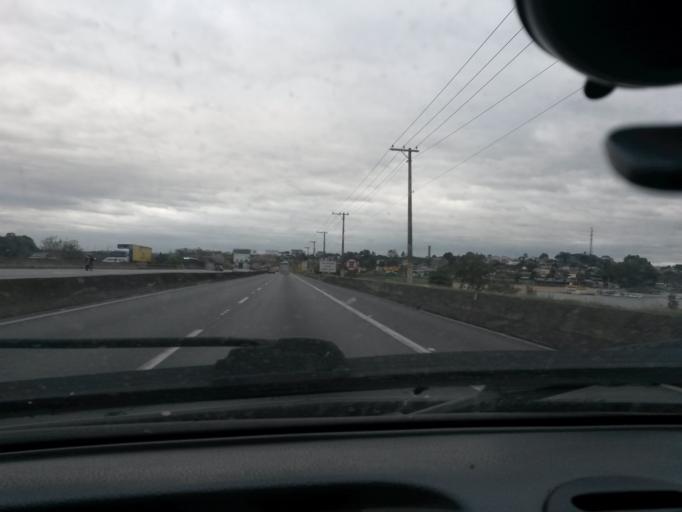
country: BR
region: Sao Paulo
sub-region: Sao Bernardo Do Campo
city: Sao Bernardo do Campo
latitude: -23.7716
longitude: -46.5329
